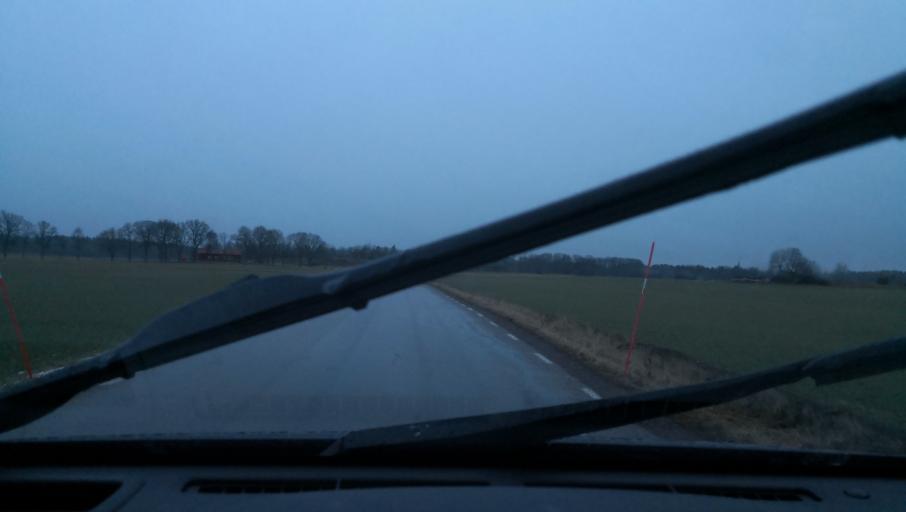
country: SE
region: Soedermanland
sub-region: Eskilstuna Kommun
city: Arla
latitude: 59.4265
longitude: 16.7095
